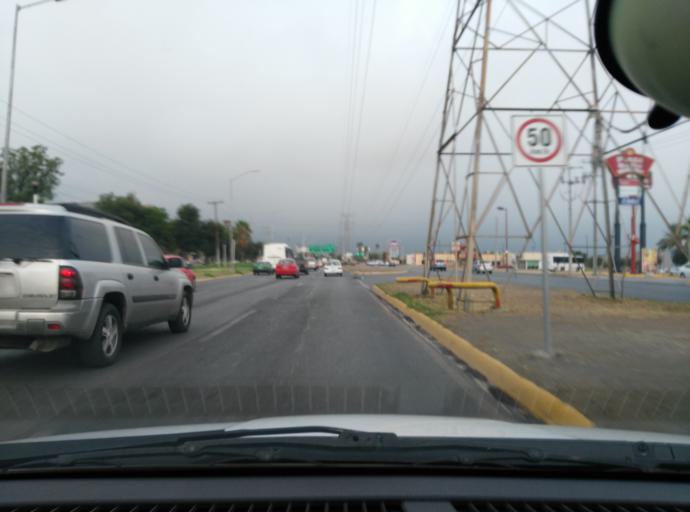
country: MX
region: Nuevo Leon
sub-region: San Nicolas de los Garza
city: San Nicolas de los Garza
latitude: 25.7698
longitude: -100.2753
